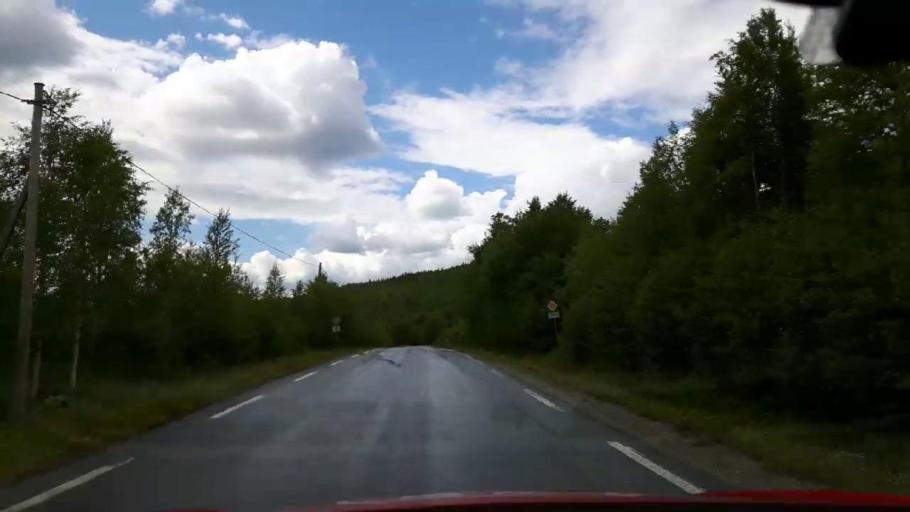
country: NO
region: Nord-Trondelag
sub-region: Lierne
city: Sandvika
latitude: 64.1167
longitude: 13.9646
